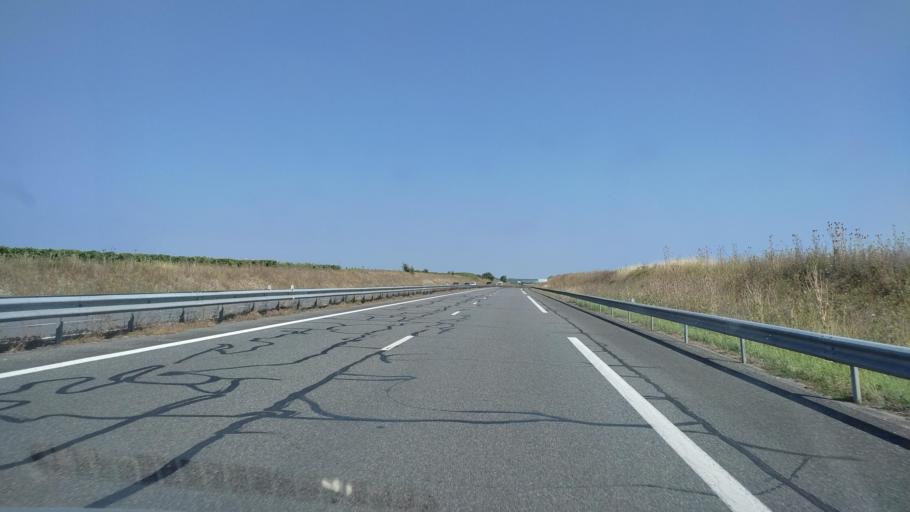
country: FR
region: Poitou-Charentes
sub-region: Departement de la Charente
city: Saint-Meme-les-Carrieres
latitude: 45.6939
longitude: -0.0989
